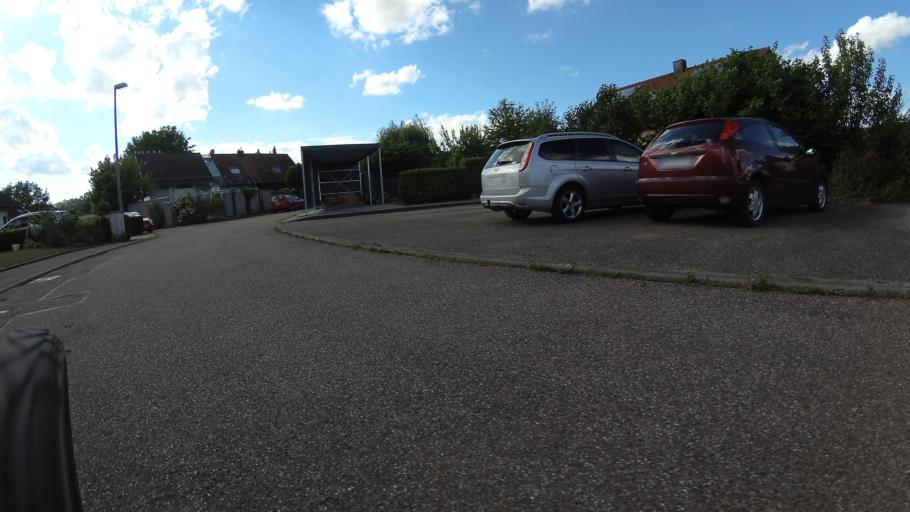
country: DE
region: Baden-Wuerttemberg
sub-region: Regierungsbezirk Stuttgart
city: Neuenstadt am Kocher
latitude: 49.2464
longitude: 9.3029
